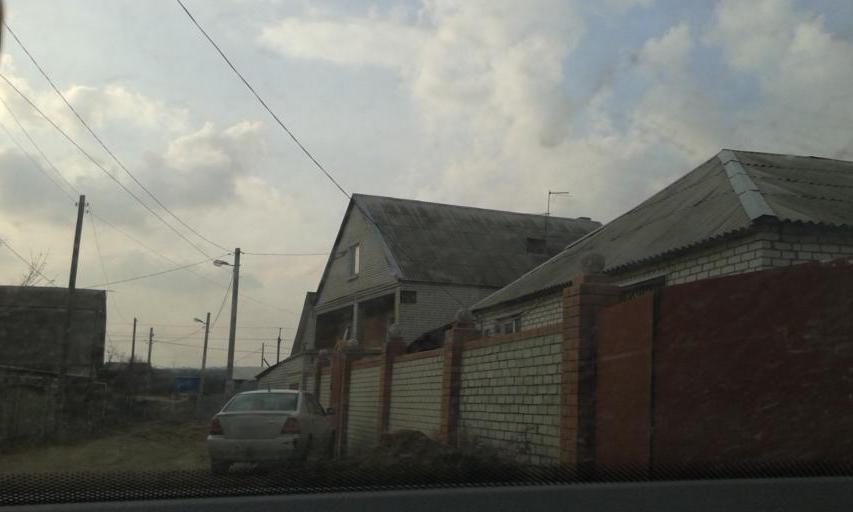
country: RU
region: Volgograd
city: Volgograd
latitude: 48.6549
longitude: 44.4146
